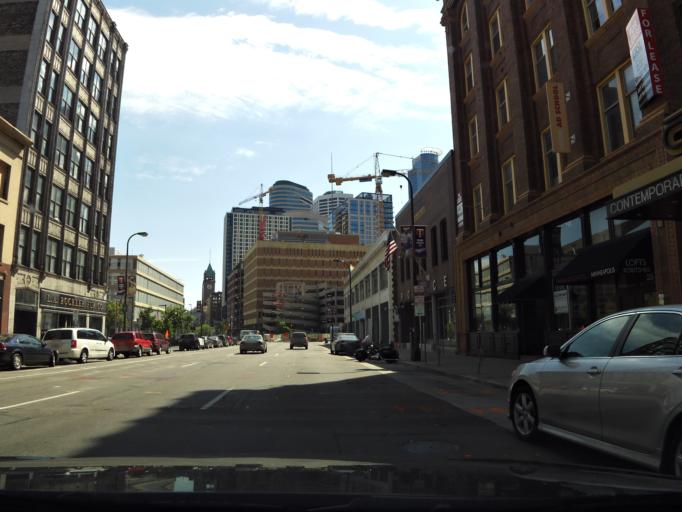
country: US
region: Minnesota
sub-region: Hennepin County
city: Minneapolis
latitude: 44.9810
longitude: -93.2723
